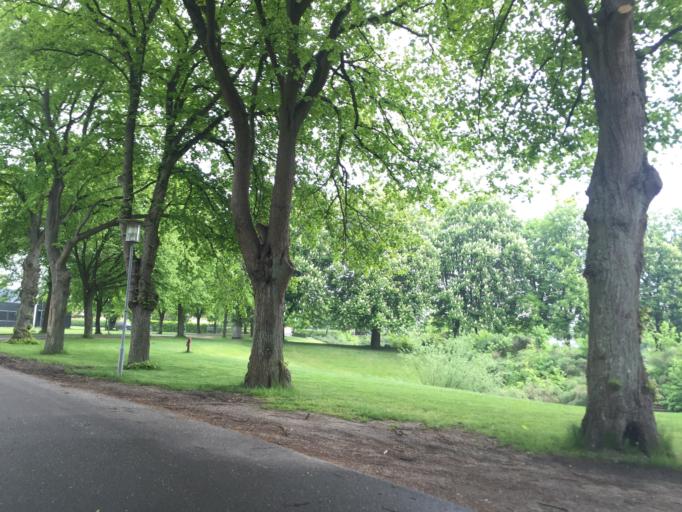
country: DK
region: Capital Region
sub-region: Rodovre Kommune
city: Rodovre
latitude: 55.6773
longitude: 12.4407
